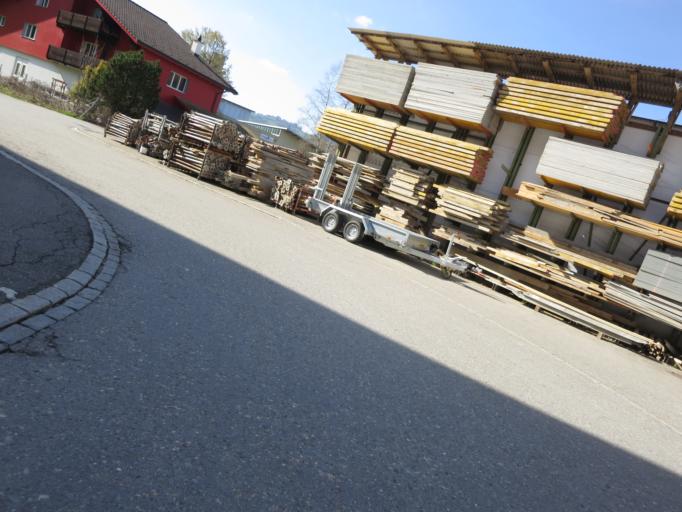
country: CH
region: Zurich
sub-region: Bezirk Hinwil
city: Wald
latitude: 47.2641
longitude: 8.9204
